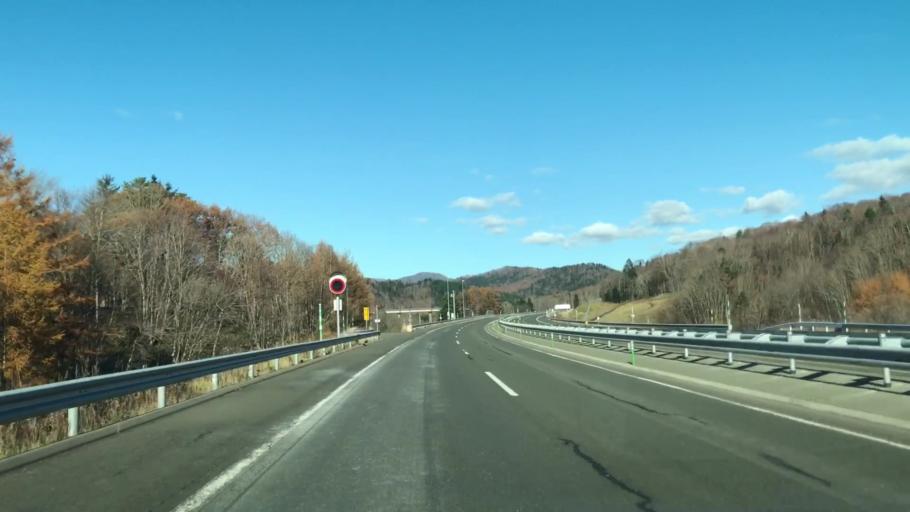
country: JP
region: Hokkaido
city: Shimo-furano
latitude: 42.9325
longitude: 142.2051
